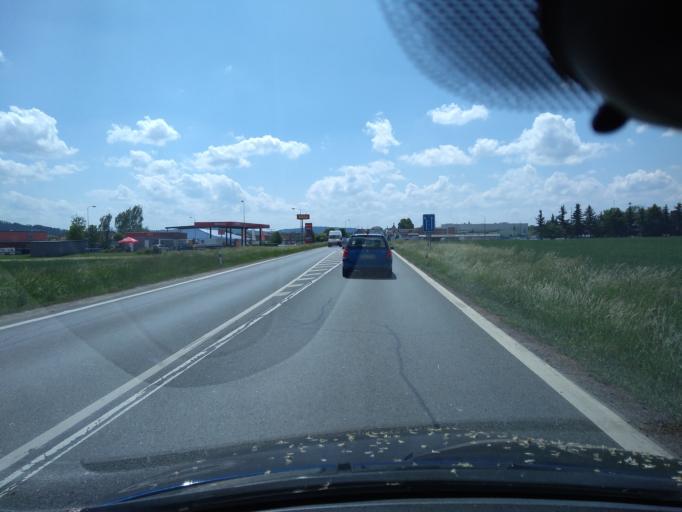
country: CZ
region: Plzensky
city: Prestice
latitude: 49.5842
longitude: 13.3267
